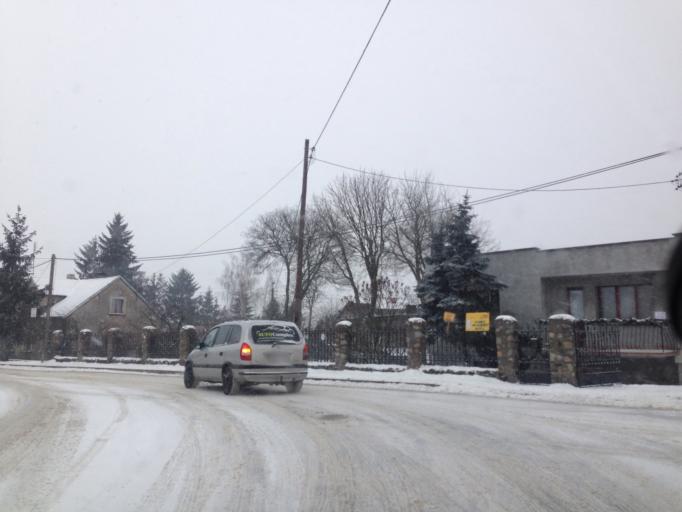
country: PL
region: Kujawsko-Pomorskie
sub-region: Powiat brodnicki
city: Brodnica
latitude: 53.2443
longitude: 19.4005
